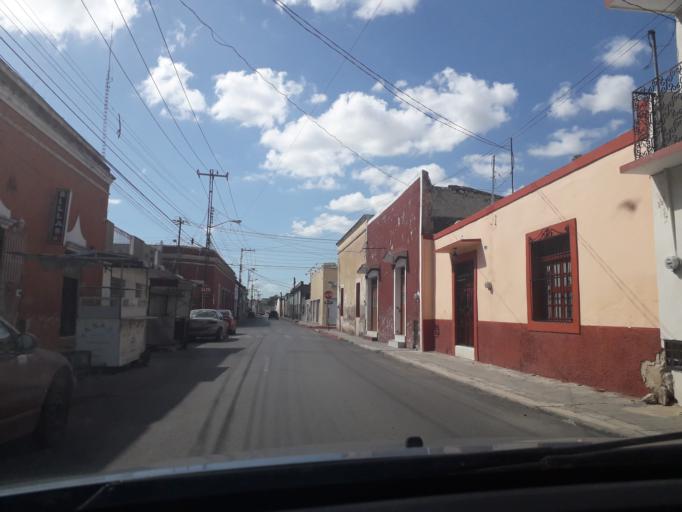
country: MX
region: Yucatan
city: Merida
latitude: 20.9599
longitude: -89.6255
